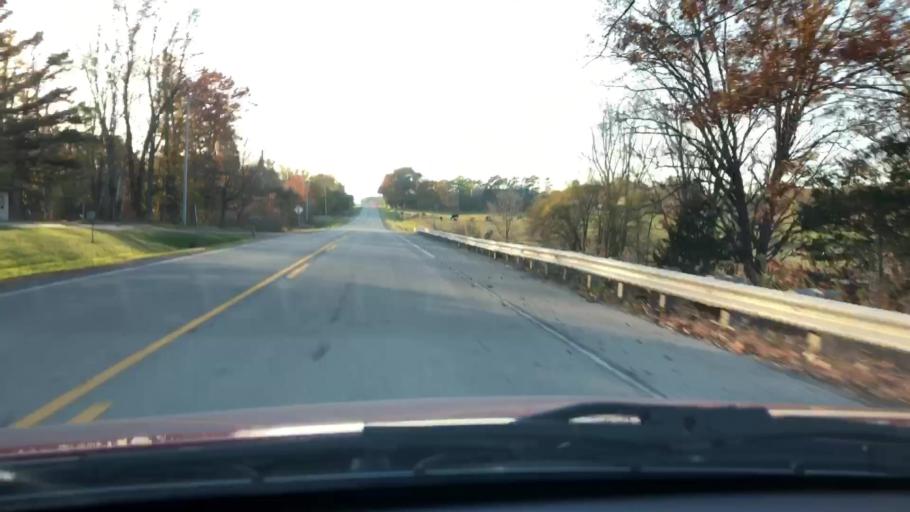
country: US
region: Wisconsin
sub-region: Brown County
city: Oneida
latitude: 44.4443
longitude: -88.2397
